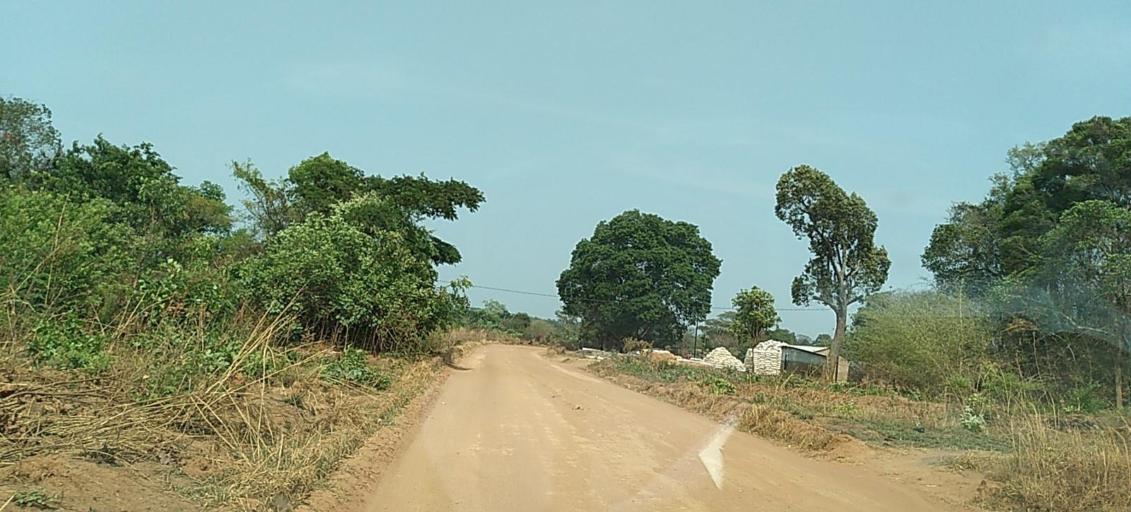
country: ZM
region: Copperbelt
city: Chililabombwe
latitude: -12.3395
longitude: 27.7183
